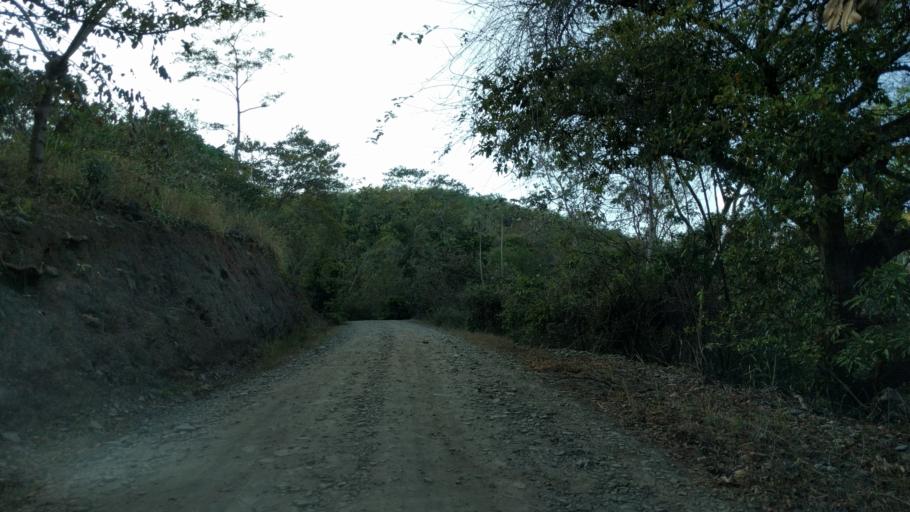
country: CR
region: Puntarenas
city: Esparza
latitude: 10.0221
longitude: -84.6986
